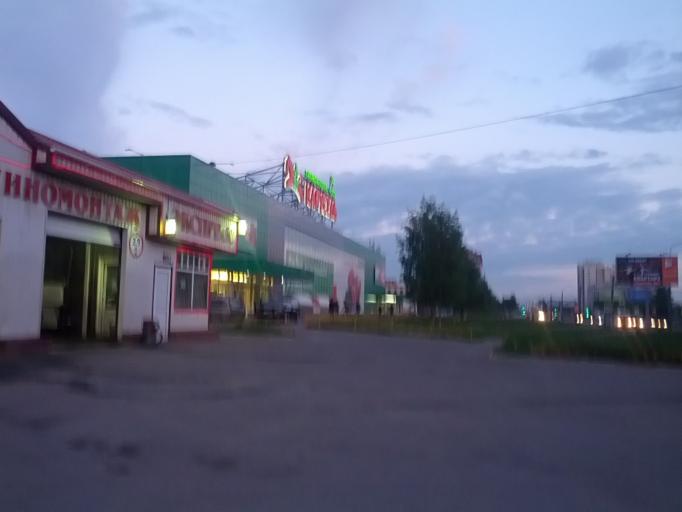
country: RU
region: Leningrad
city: Rybatskoye
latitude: 59.8964
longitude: 30.4924
